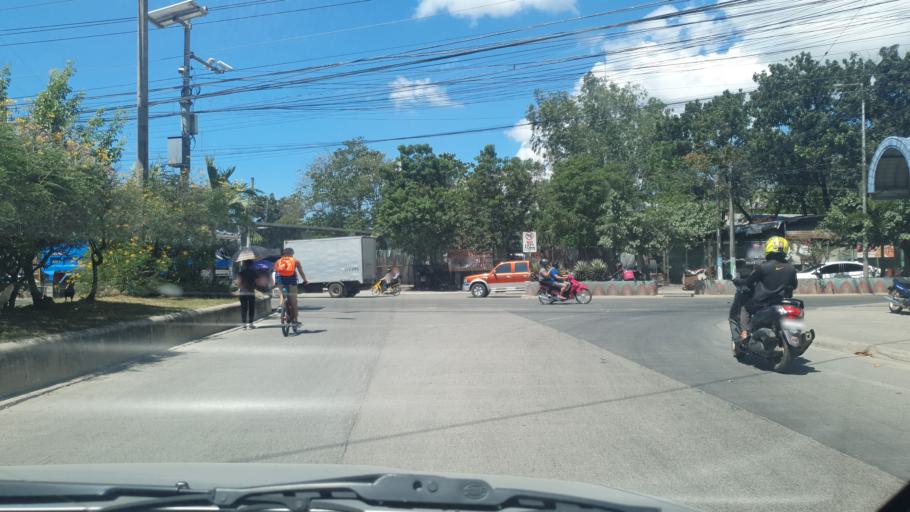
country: PH
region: Central Visayas
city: Mandaue City
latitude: 10.3207
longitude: 123.9263
